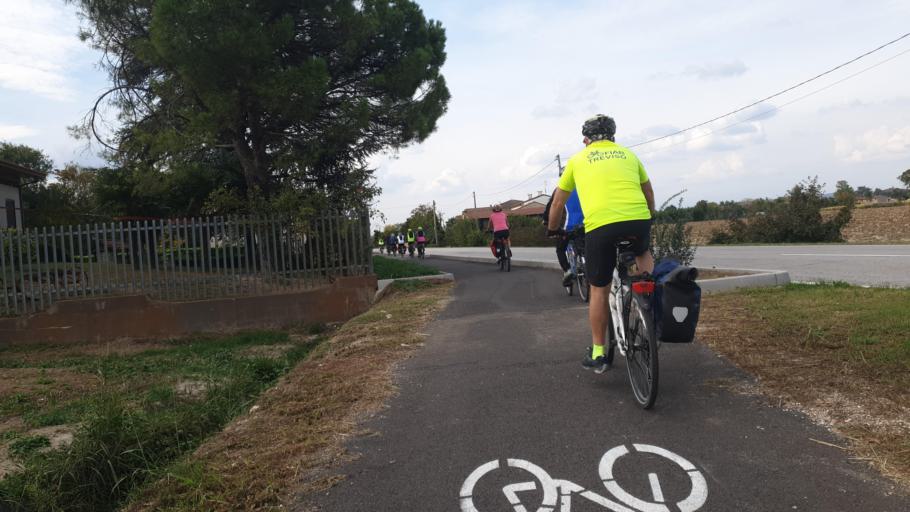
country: IT
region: Veneto
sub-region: Provincia di Vicenza
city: Poiana Maggiore
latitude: 45.2868
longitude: 11.5178
